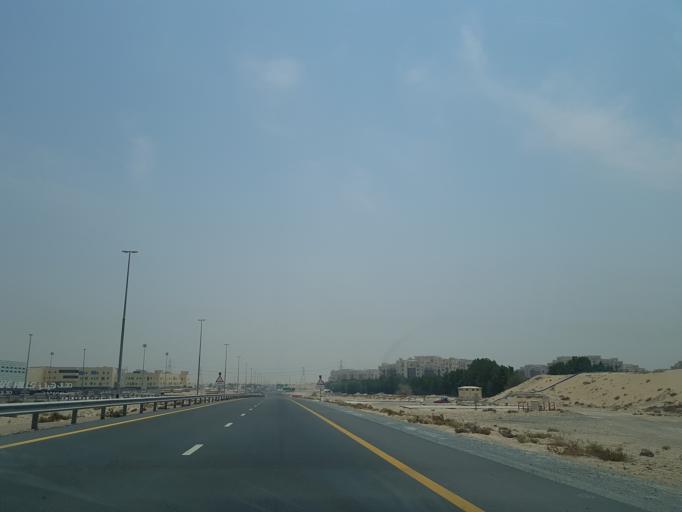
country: AE
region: Dubai
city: Dubai
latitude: 25.0119
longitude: 55.2509
